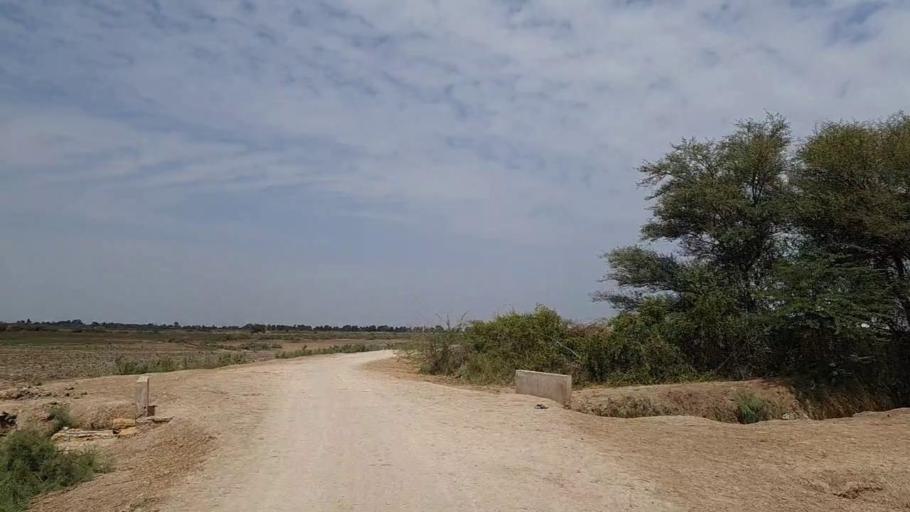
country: PK
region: Sindh
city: Daro Mehar
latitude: 24.7858
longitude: 68.2055
